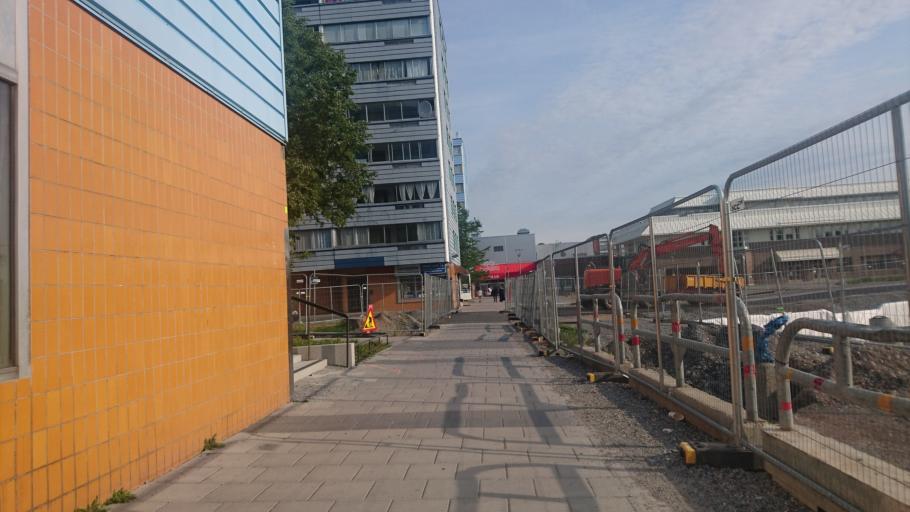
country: SE
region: Stockholm
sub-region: Upplands Vasby Kommun
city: Upplands Vaesby
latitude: 59.5170
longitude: 17.9116
